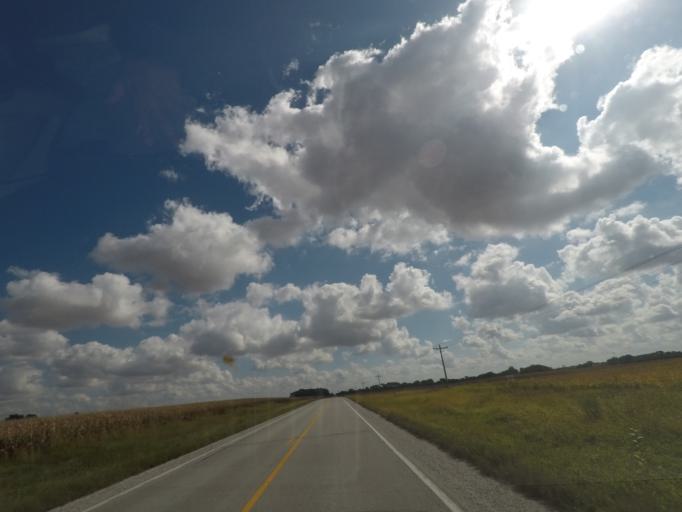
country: US
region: Iowa
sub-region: Story County
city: Nevada
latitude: 42.0226
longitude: -93.3627
